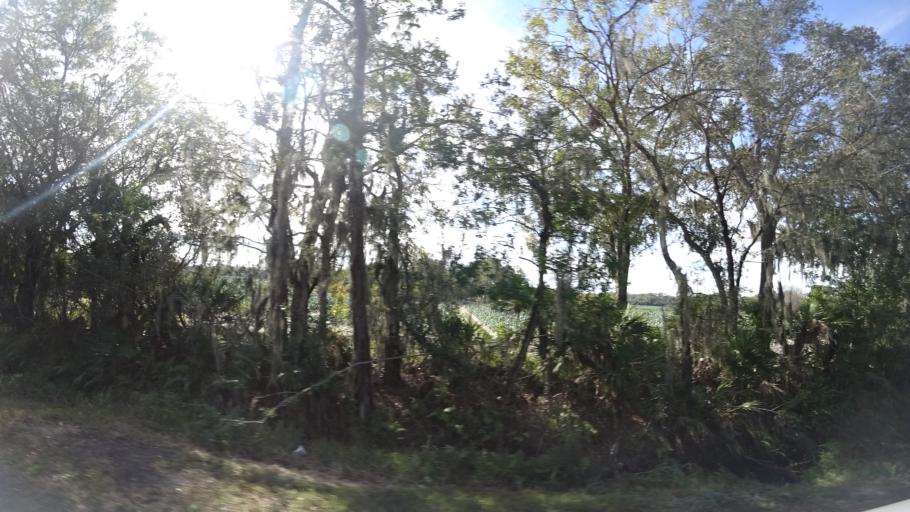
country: US
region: Florida
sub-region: Hillsborough County
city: Ruskin
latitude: 27.6305
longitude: -82.4390
